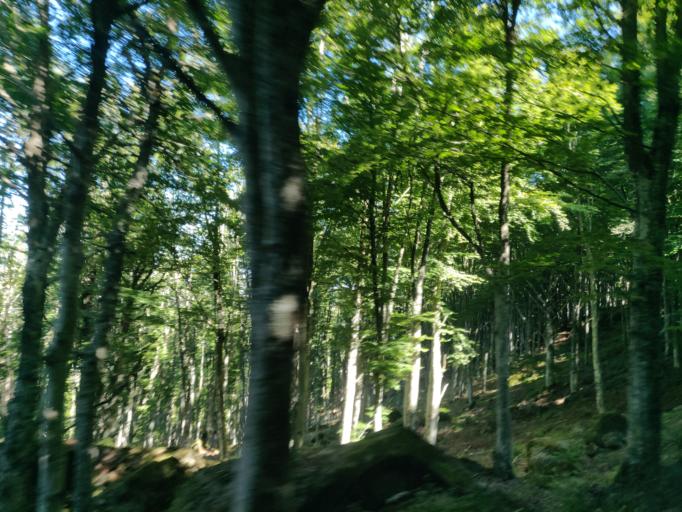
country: IT
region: Tuscany
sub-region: Provincia di Siena
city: Abbadia San Salvatore
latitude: 42.8950
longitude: 11.6307
